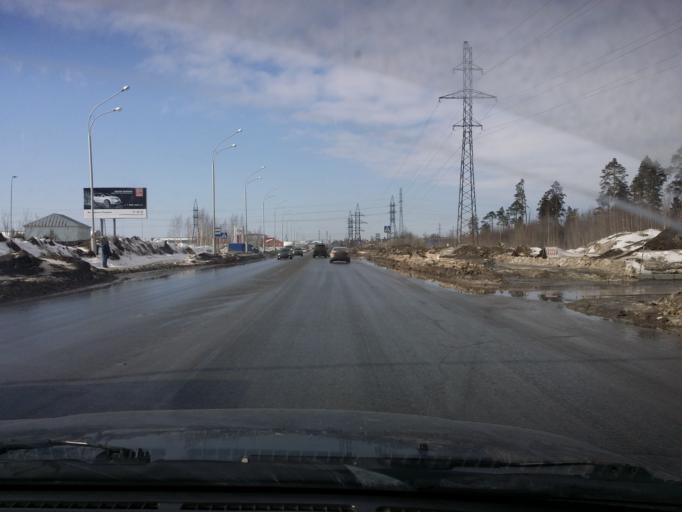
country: RU
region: Khanty-Mansiyskiy Avtonomnyy Okrug
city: Nizhnevartovsk
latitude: 60.9633
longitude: 76.5524
